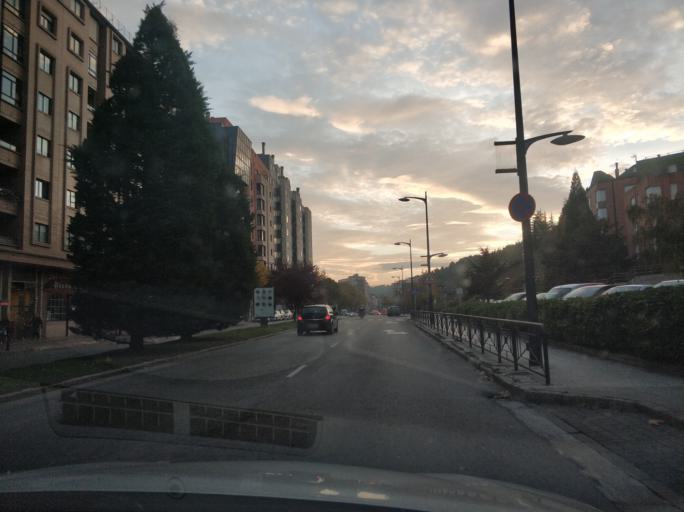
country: ES
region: Castille and Leon
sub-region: Provincia de Burgos
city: Burgos
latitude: 42.3539
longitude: -3.6923
